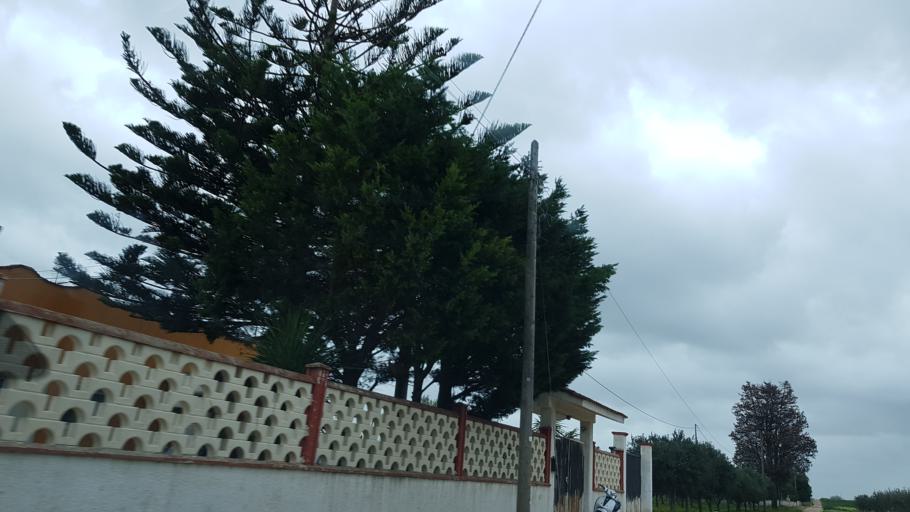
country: IT
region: Apulia
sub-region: Provincia di Brindisi
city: Brindisi
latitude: 40.6669
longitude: 17.8655
